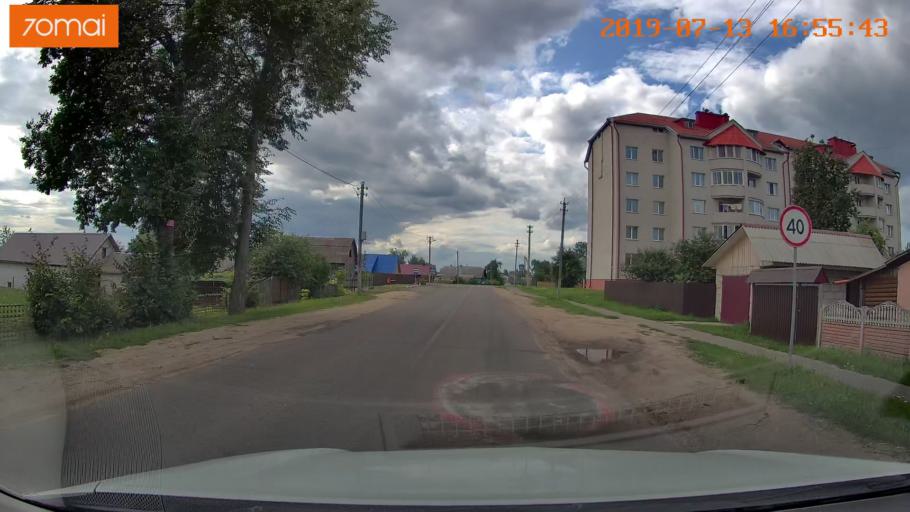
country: BY
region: Mogilev
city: Kirawsk
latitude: 53.2690
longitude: 29.4648
